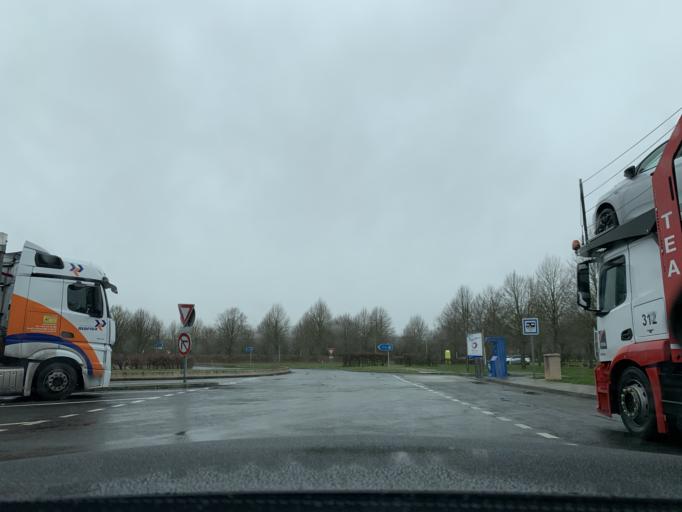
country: FR
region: Picardie
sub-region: Departement de l'Oise
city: Breteuil
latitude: 49.6095
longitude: 2.2041
